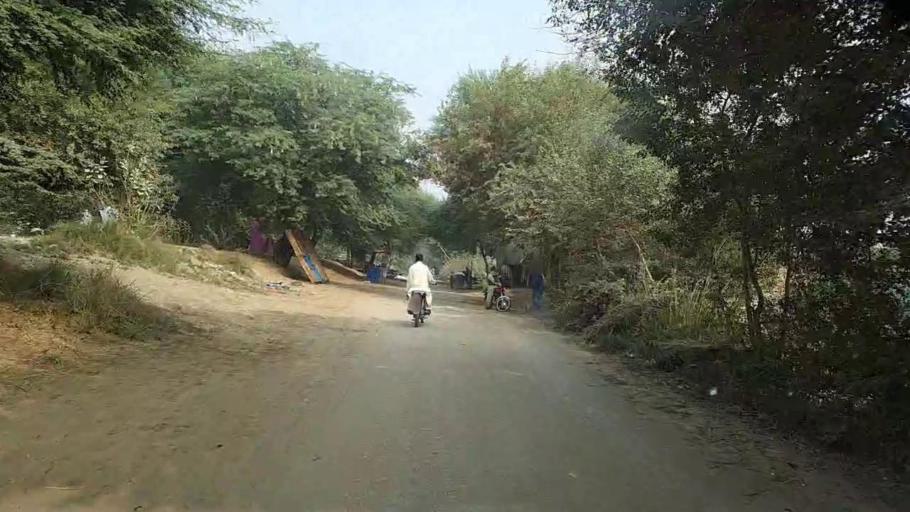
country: PK
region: Sindh
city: Bozdar
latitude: 27.0642
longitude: 68.6147
